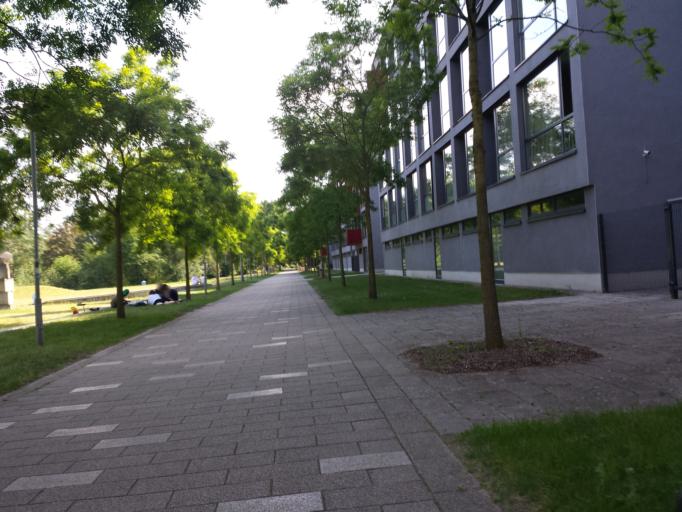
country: DE
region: Bremen
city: Bremen
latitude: 53.1077
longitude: 8.8498
